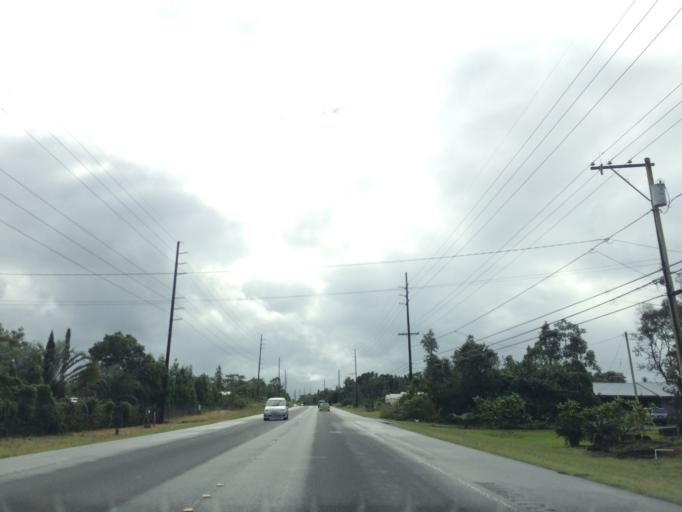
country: US
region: Hawaii
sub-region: Hawaii County
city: Ainaloa
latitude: 19.5506
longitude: -154.9826
